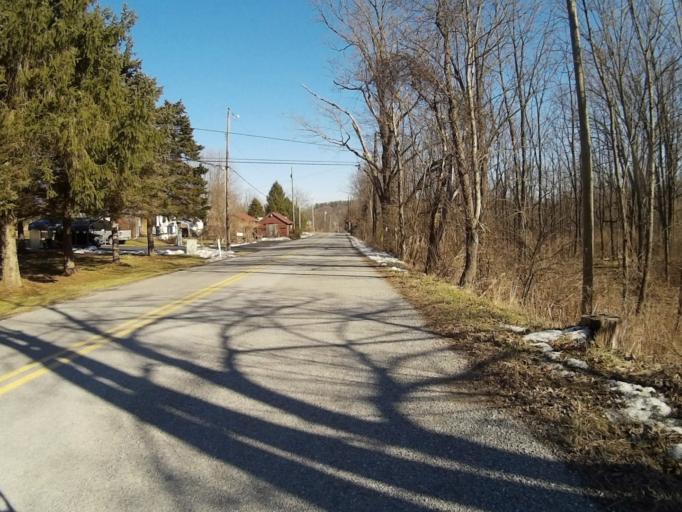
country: US
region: Pennsylvania
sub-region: Centre County
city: Houserville
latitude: 40.8748
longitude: -77.8669
